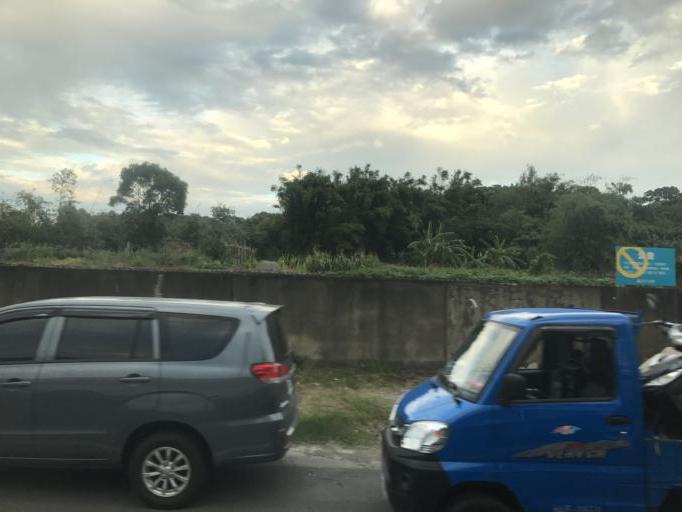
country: TW
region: Taiwan
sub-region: Hsinchu
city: Hsinchu
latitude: 24.7859
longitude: 120.9298
